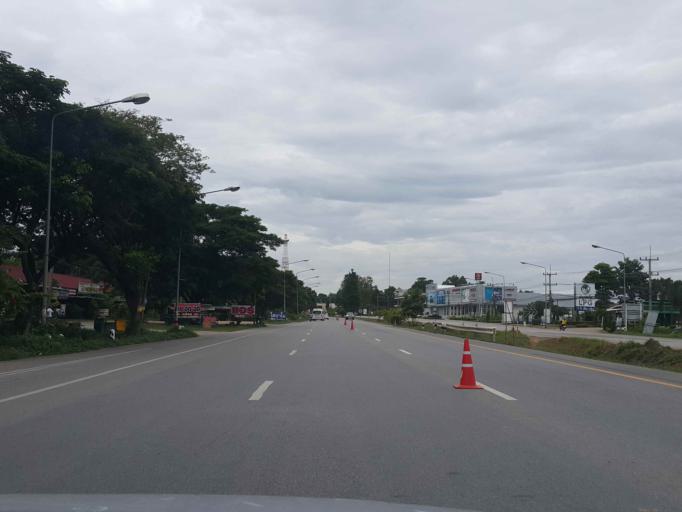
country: TH
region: Lampang
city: Thoen
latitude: 17.6175
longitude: 99.2327
